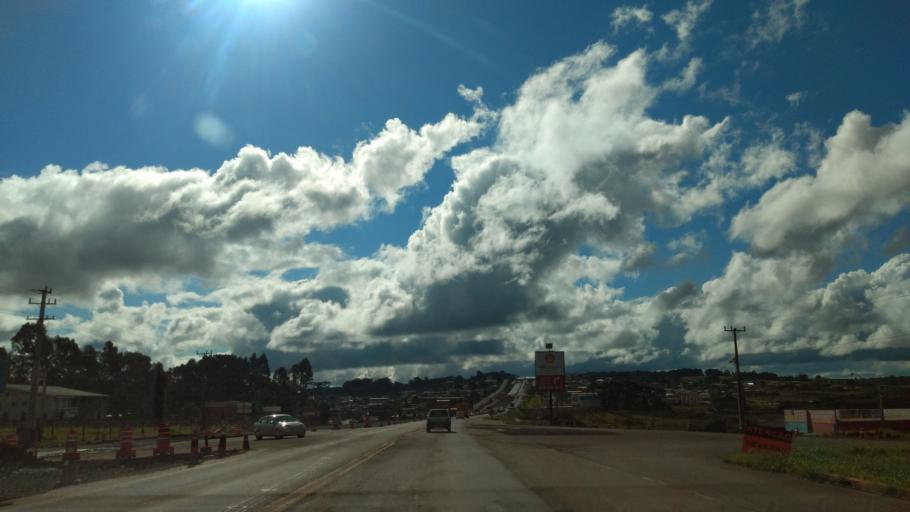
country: BR
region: Parana
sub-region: Guarapuava
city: Guarapuava
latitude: -25.3573
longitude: -51.4825
